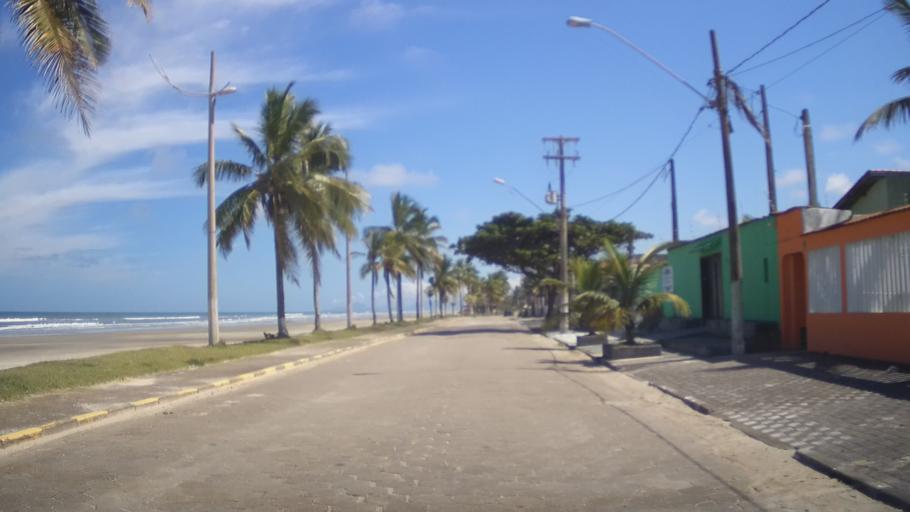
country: BR
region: Sao Paulo
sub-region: Itanhaem
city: Itanhaem
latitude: -24.1413
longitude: -46.7069
